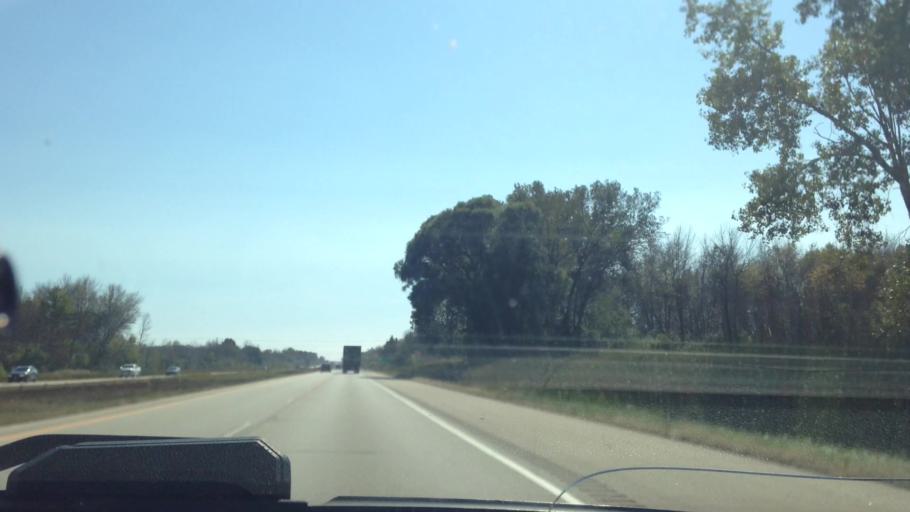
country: US
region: Wisconsin
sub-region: Ozaukee County
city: Grafton
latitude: 43.2693
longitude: -87.9201
